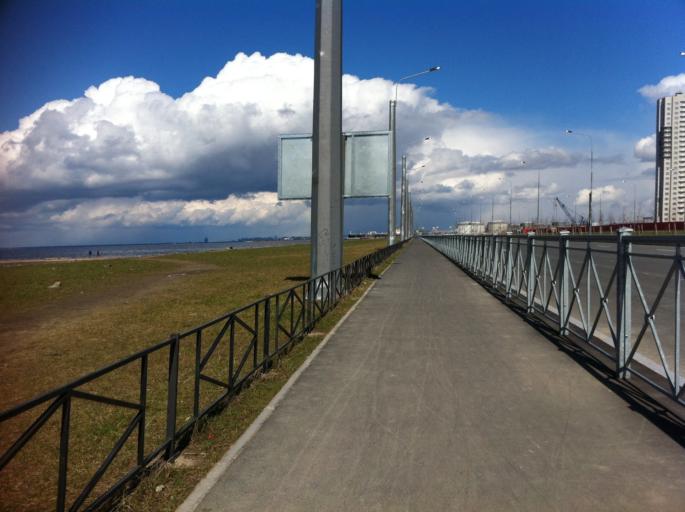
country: RU
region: St.-Petersburg
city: Sosnovaya Polyana
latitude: 59.8680
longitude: 30.1534
